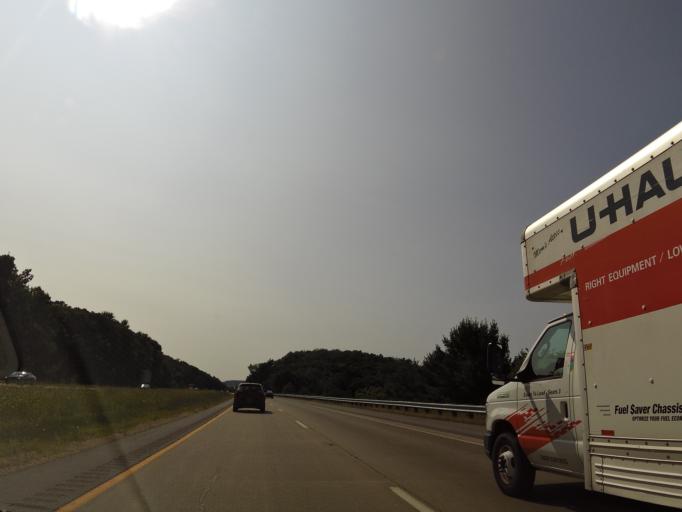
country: US
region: Wisconsin
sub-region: Monroe County
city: Tomah
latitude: 43.9529
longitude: -90.5265
